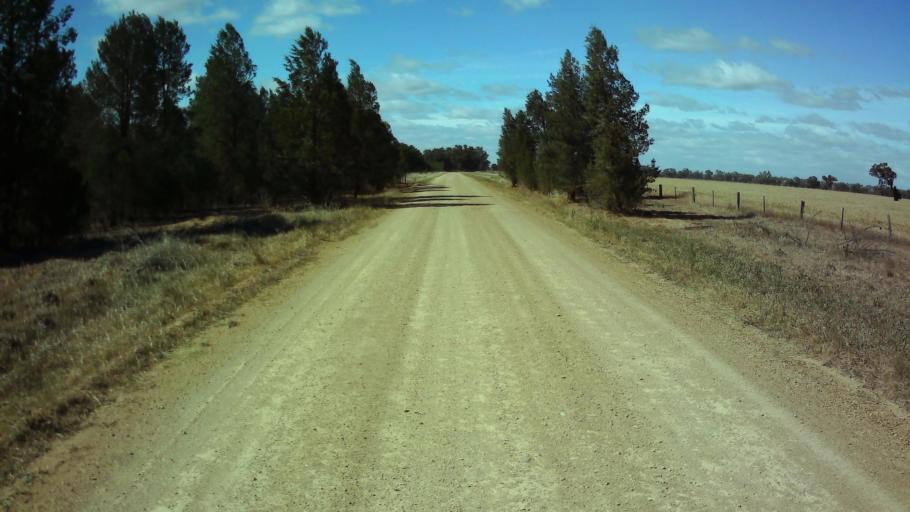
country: AU
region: New South Wales
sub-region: Weddin
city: Grenfell
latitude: -34.0315
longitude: 148.3173
